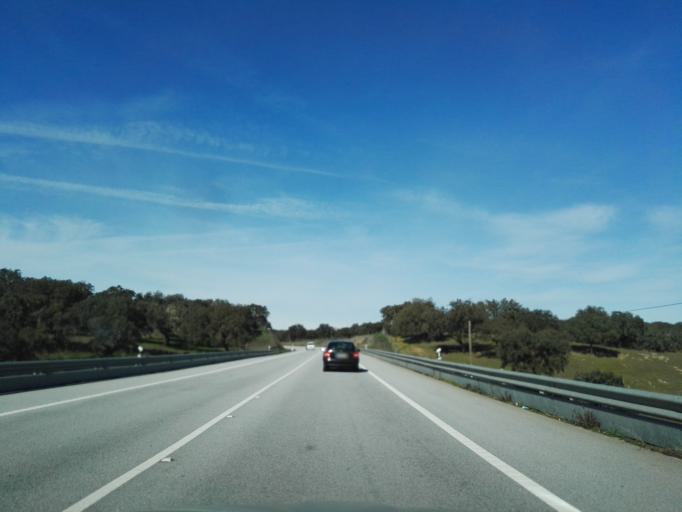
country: PT
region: Portalegre
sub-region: Portalegre
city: Alegrete
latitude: 39.1831
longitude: -7.3452
